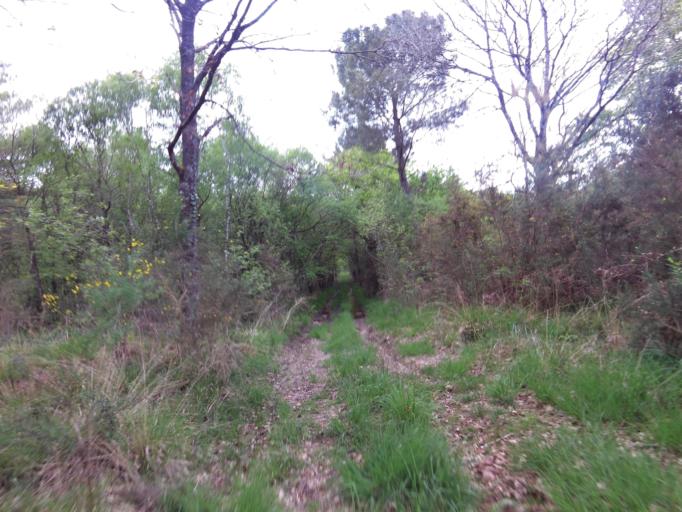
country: FR
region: Brittany
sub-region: Departement du Morbihan
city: Molac
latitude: 47.7499
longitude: -2.4245
